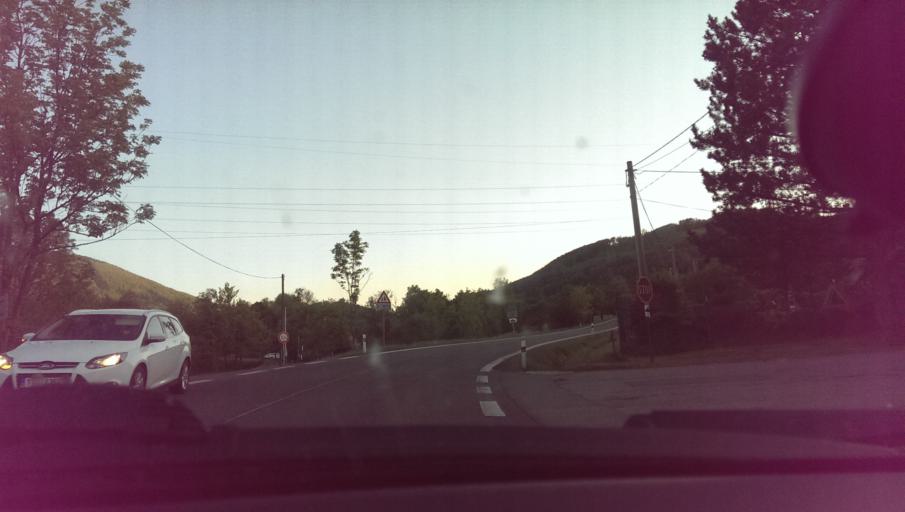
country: CZ
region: Moravskoslezsky
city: Frenstat pod Radhostem
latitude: 49.5216
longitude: 18.2036
